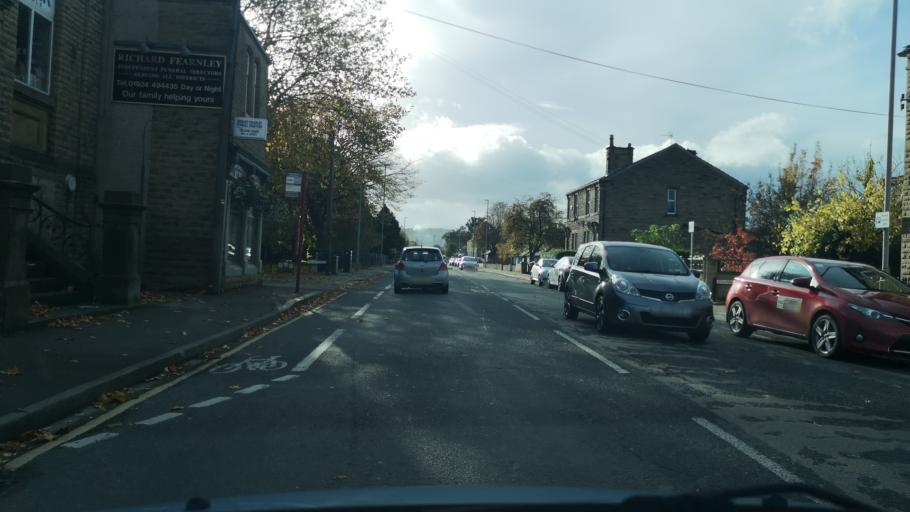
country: GB
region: England
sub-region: Kirklees
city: Mirfield
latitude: 53.6777
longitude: -1.6678
